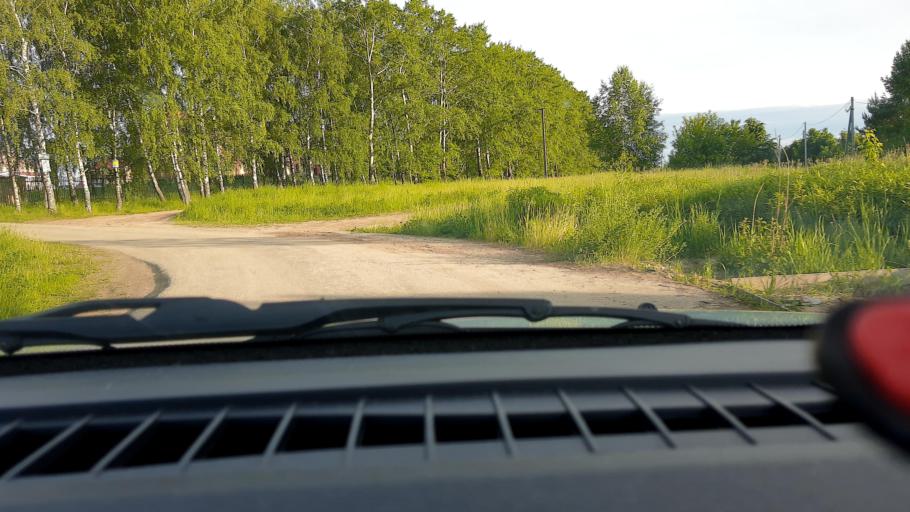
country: RU
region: Nizjnij Novgorod
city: Afonino
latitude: 56.1207
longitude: 44.0251
